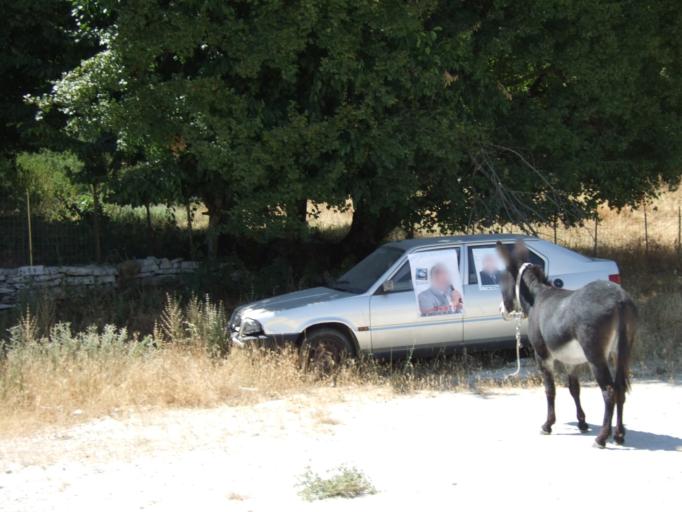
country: GR
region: Epirus
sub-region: Nomos Ioanninon
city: Asprangeloi
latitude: 39.8823
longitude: 20.7435
